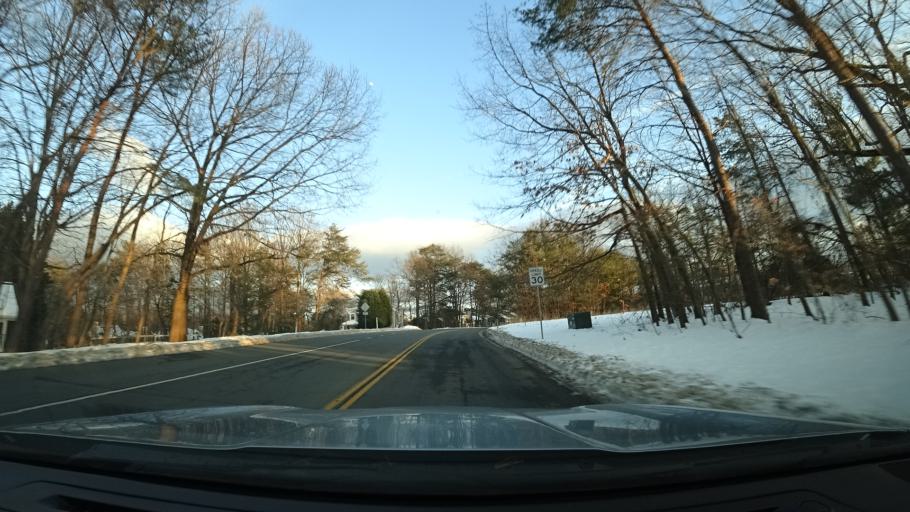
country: US
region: Virginia
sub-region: Fairfax County
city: Reston
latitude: 38.9803
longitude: -77.3552
